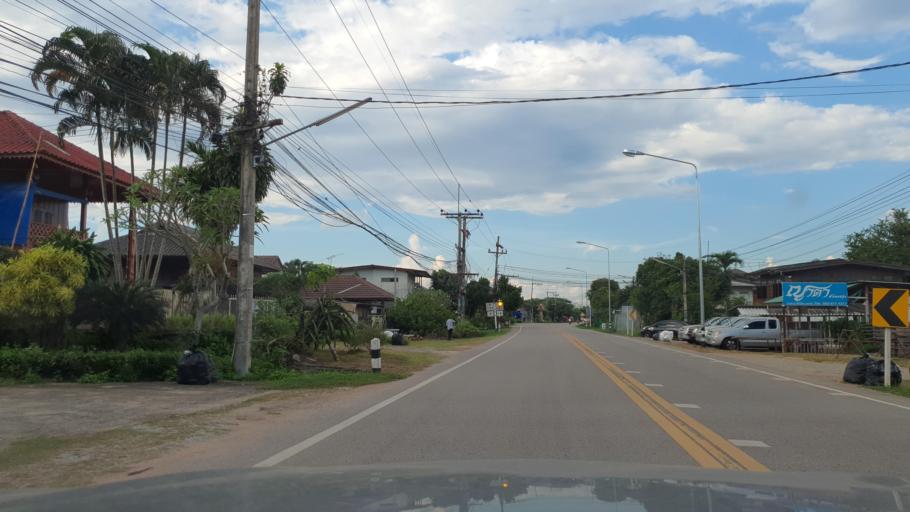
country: TH
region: Phayao
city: Phayao
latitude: 19.1801
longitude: 99.8363
